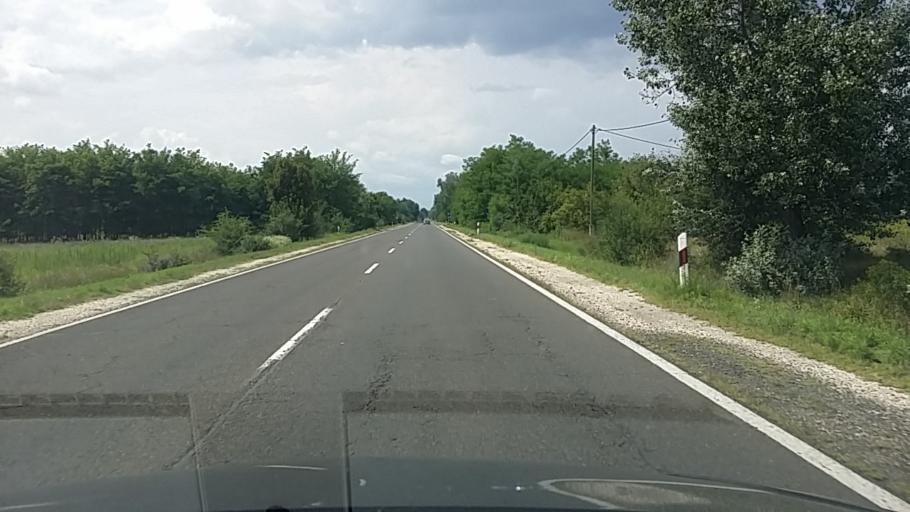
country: HU
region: Pest
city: Taborfalva
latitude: 47.0727
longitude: 19.4950
